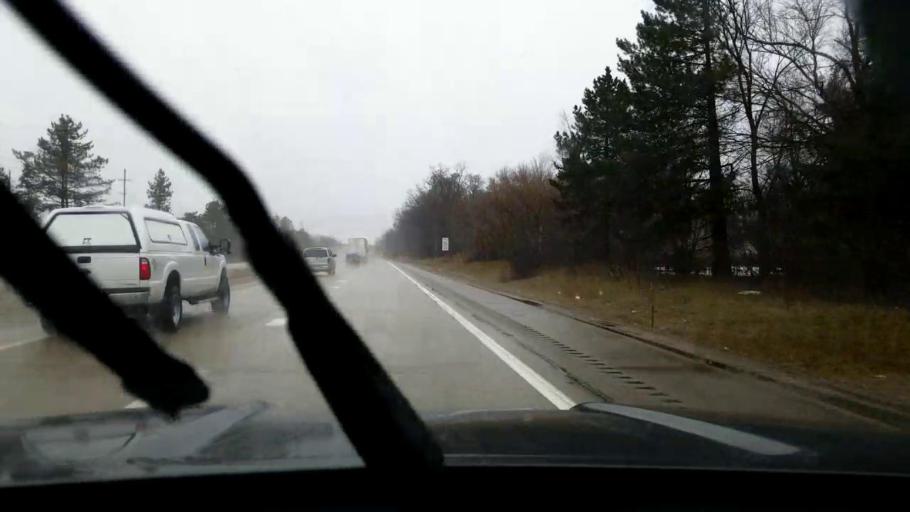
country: US
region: Michigan
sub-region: Jackson County
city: Michigan Center
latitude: 42.2644
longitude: -84.3573
